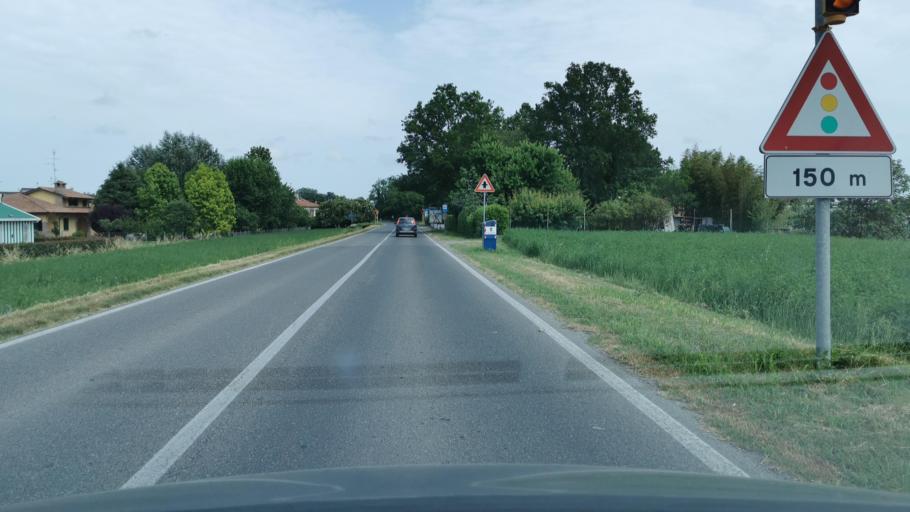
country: IT
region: Emilia-Romagna
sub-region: Provincia di Ravenna
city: Sant'Alberto
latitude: 44.5374
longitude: 12.1589
